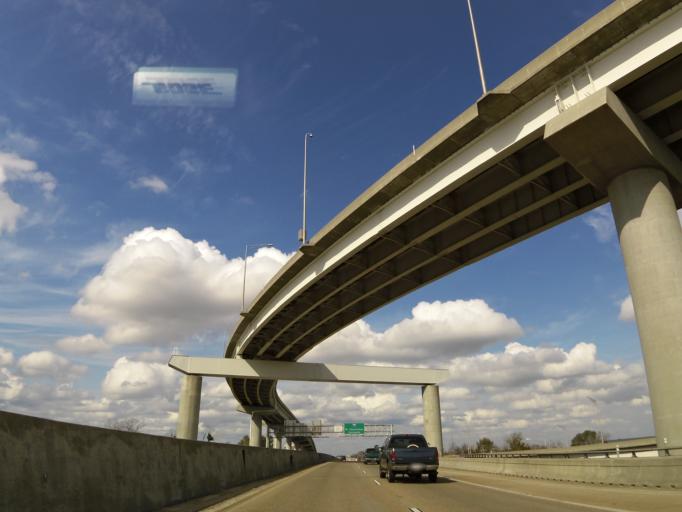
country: US
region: South Carolina
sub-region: Charleston County
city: Charleston
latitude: 32.8033
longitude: -79.9478
